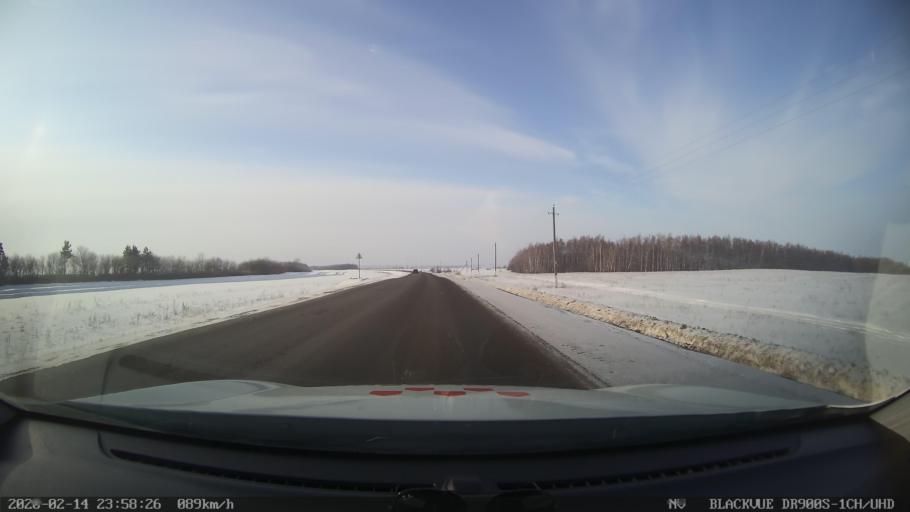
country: RU
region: Tatarstan
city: Kuybyshevskiy Zaton
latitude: 55.3407
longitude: 49.0876
